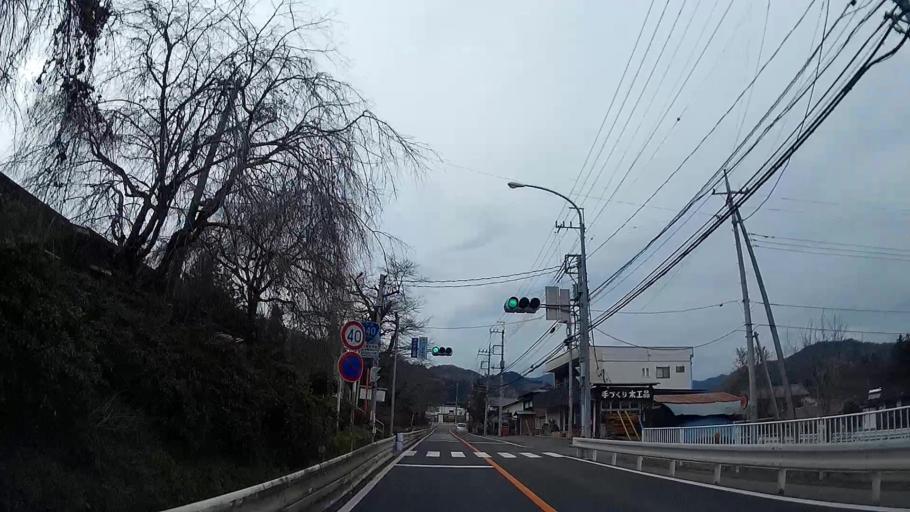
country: JP
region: Saitama
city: Chichibu
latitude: 35.9542
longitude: 139.0215
